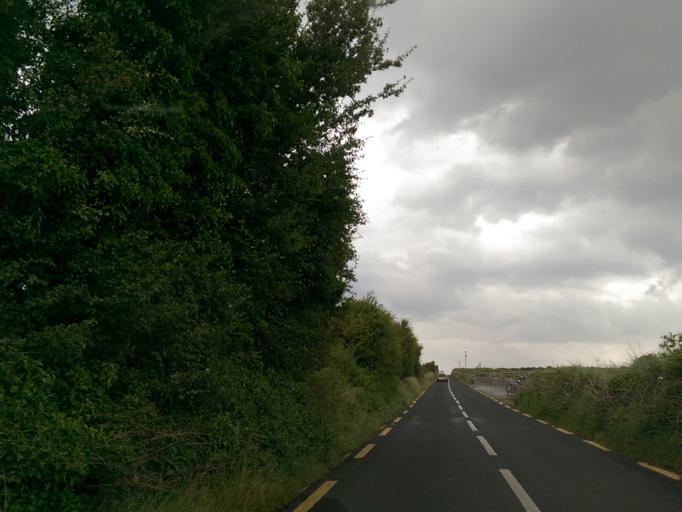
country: IE
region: Connaught
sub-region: County Galway
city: Gaillimh
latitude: 53.1243
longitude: -9.0699
